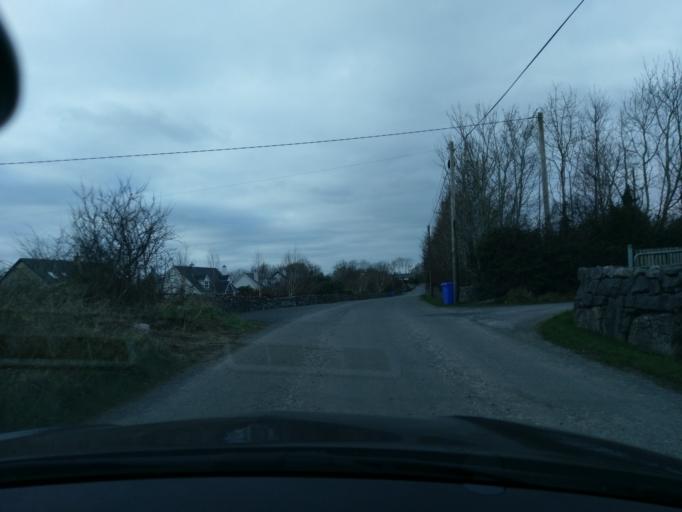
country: IE
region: Connaught
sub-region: County Galway
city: Oranmore
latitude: 53.2149
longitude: -8.8369
